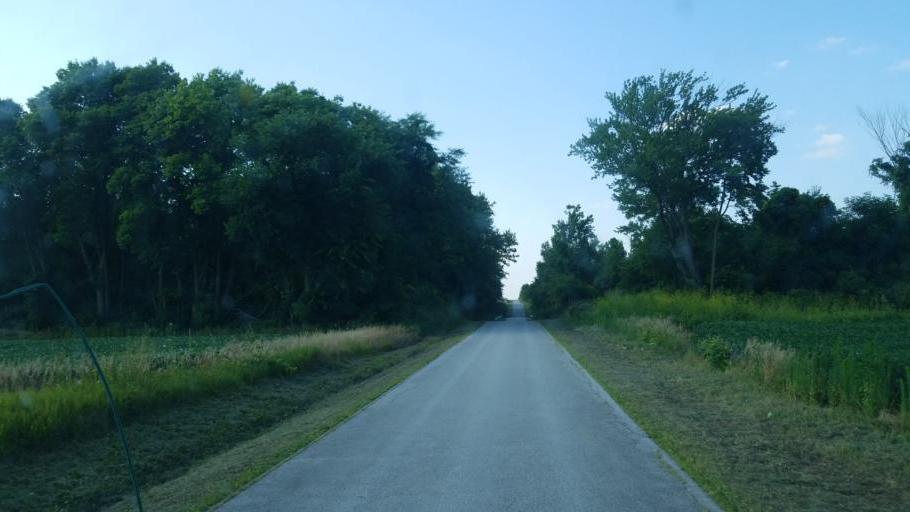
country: US
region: Ohio
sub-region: Crawford County
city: Bucyrus
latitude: 40.8527
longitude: -83.0739
